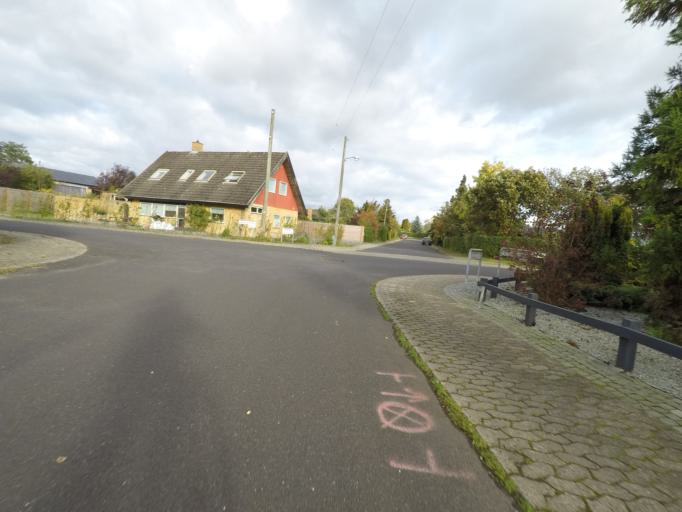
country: DK
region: Capital Region
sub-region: Ballerup Kommune
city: Ballerup
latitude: 55.7492
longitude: 12.3899
